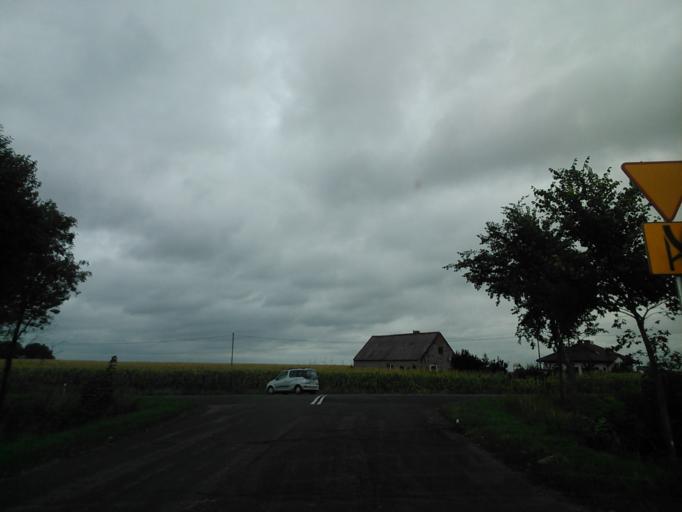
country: PL
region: Kujawsko-Pomorskie
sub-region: Powiat radziejowski
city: Piotrkow Kujawski
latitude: 52.6132
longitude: 18.4173
